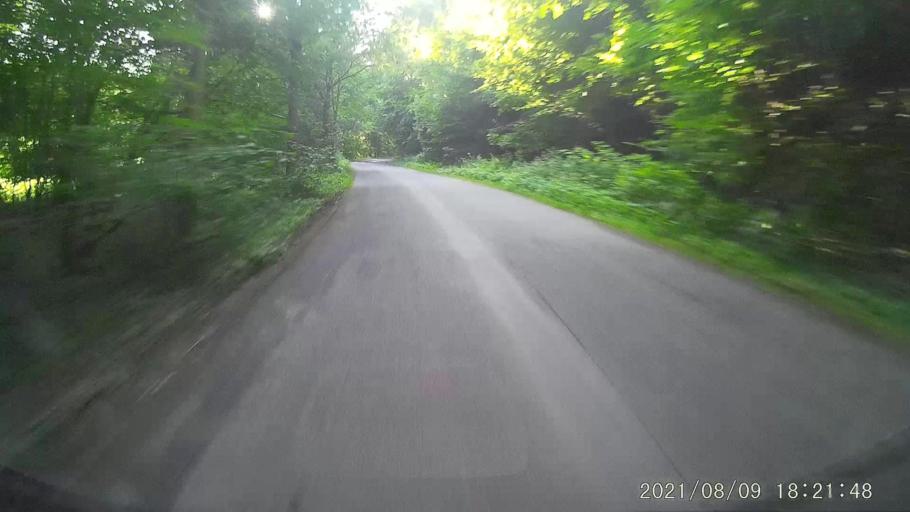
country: PL
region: Lower Silesian Voivodeship
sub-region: Powiat zabkowicki
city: Bardo
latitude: 50.5074
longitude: 16.7033
